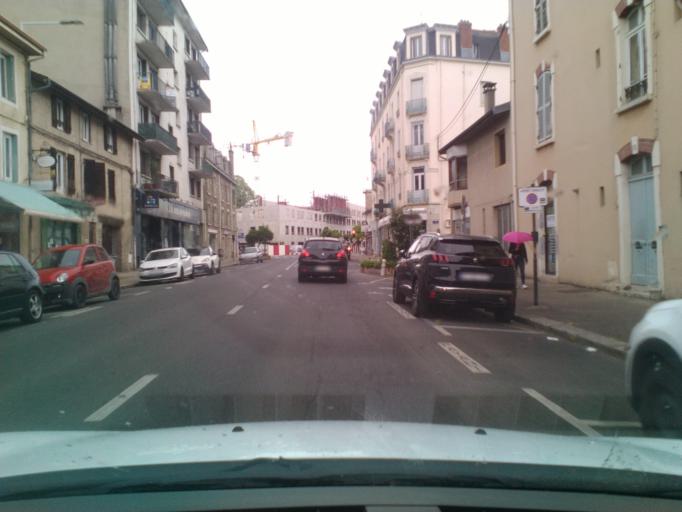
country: FR
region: Rhone-Alpes
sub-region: Departement de l'Ain
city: Bourg-en-Bresse
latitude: 46.1999
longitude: 5.2185
